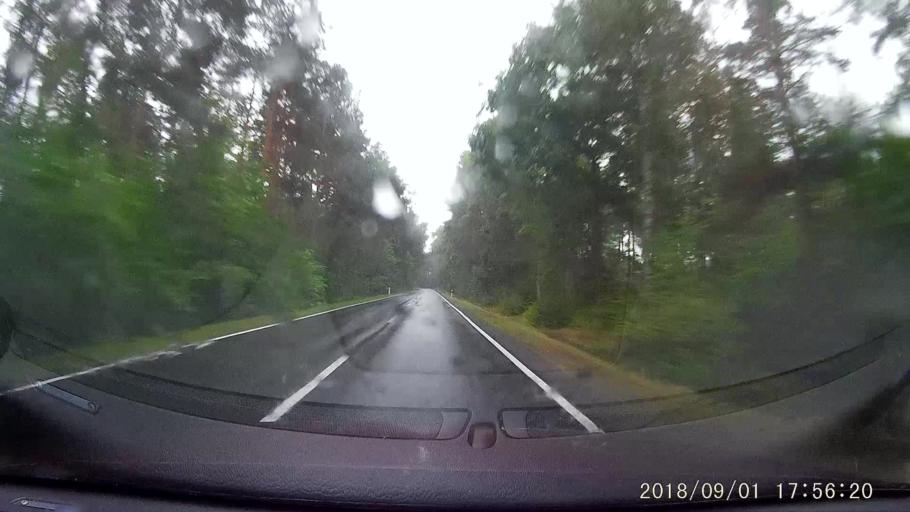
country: PL
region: Lubusz
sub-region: Powiat zaganski
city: Ilowa
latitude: 51.4463
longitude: 15.1982
